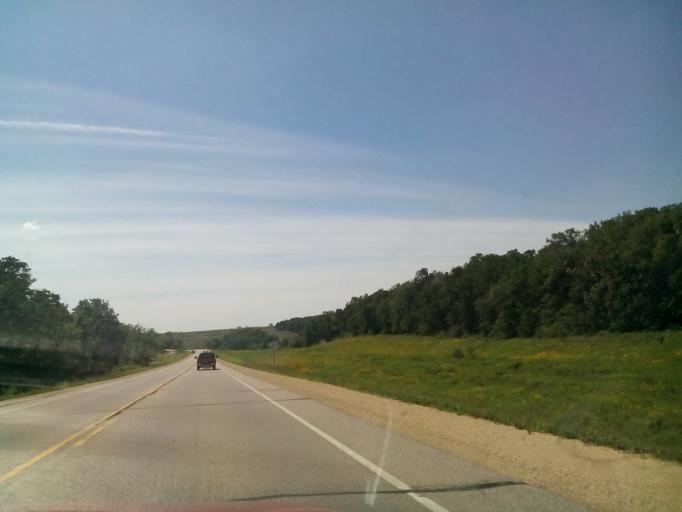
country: US
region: Wisconsin
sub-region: Green County
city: New Glarus
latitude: 42.7794
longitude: -89.6280
